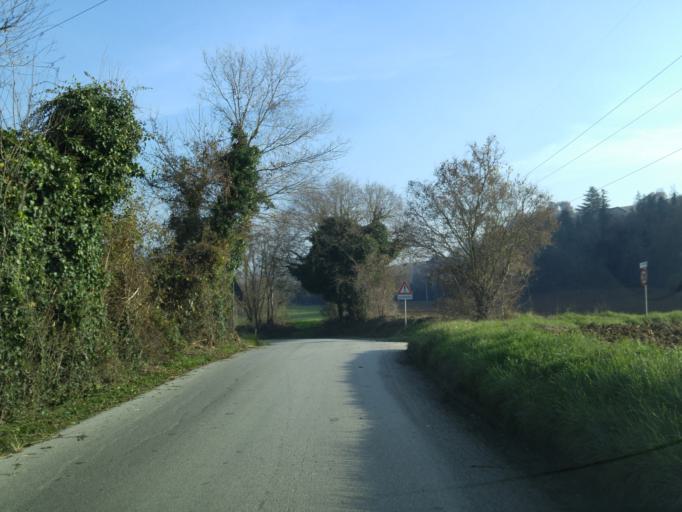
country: IT
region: The Marches
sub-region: Provincia di Pesaro e Urbino
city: Villanova
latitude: 43.7202
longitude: 12.9118
